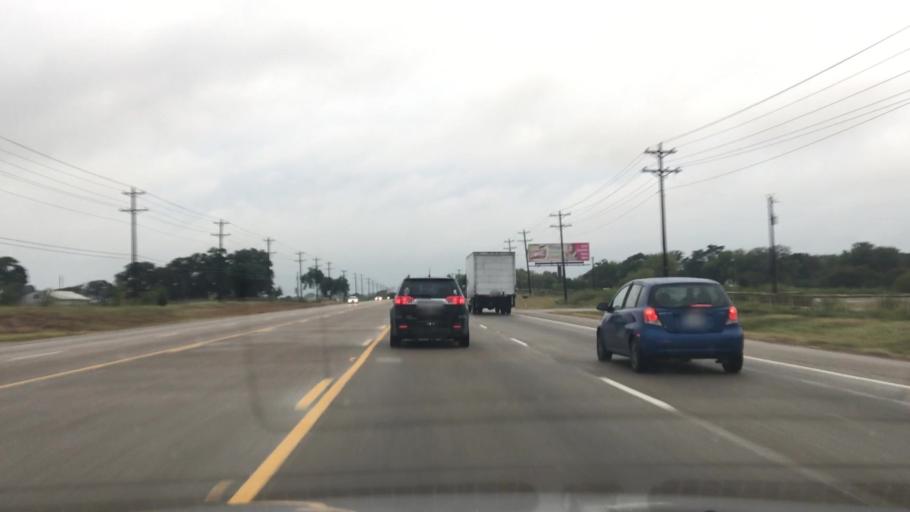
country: US
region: Texas
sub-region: Denton County
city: Cross Roads
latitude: 33.2216
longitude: -96.9526
